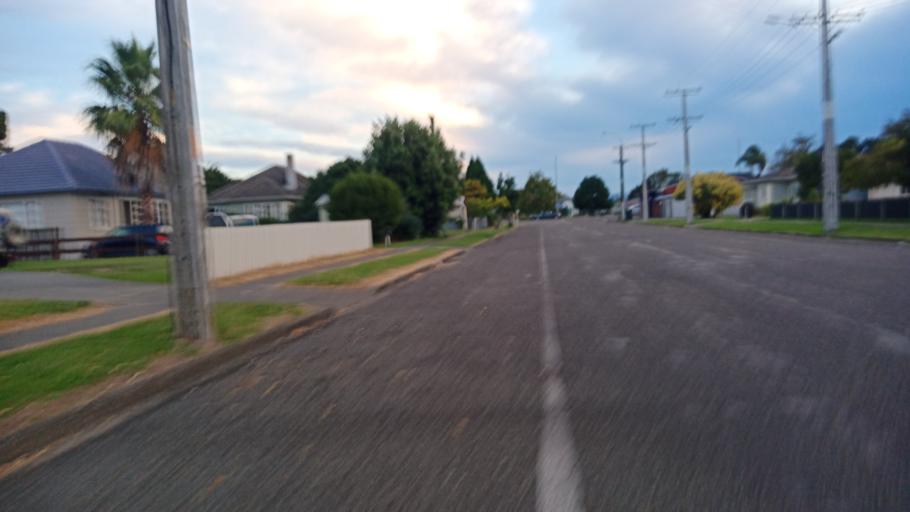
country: NZ
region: Gisborne
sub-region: Gisborne District
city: Gisborne
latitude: -38.6517
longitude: 178.0014
